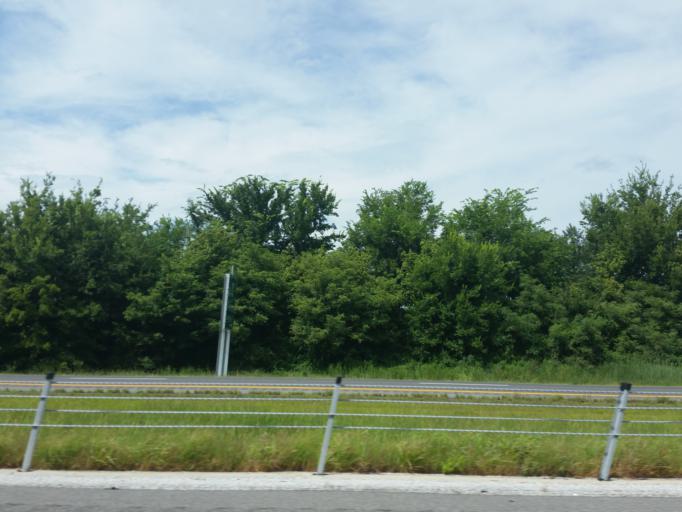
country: US
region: Kentucky
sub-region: Livingston County
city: Ledbetter
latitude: 36.9944
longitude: -88.4820
